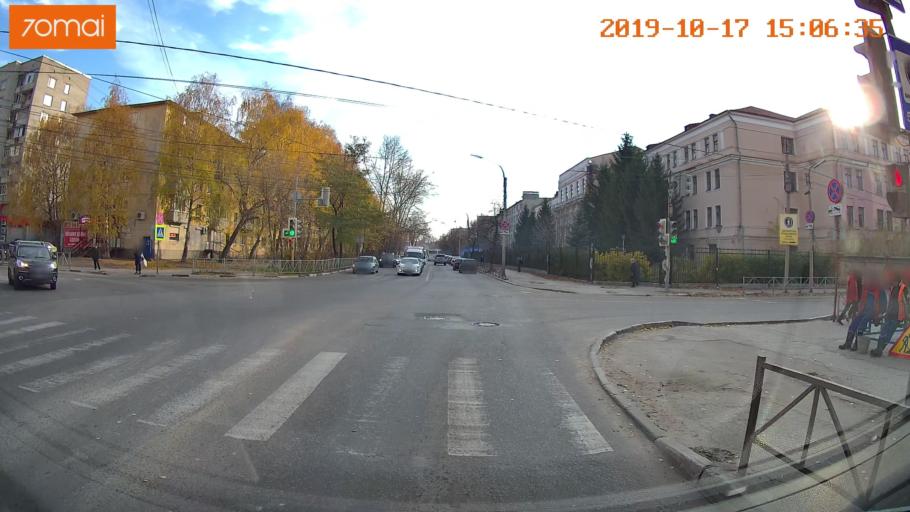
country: RU
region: Rjazan
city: Ryazan'
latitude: 54.6329
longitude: 39.7243
